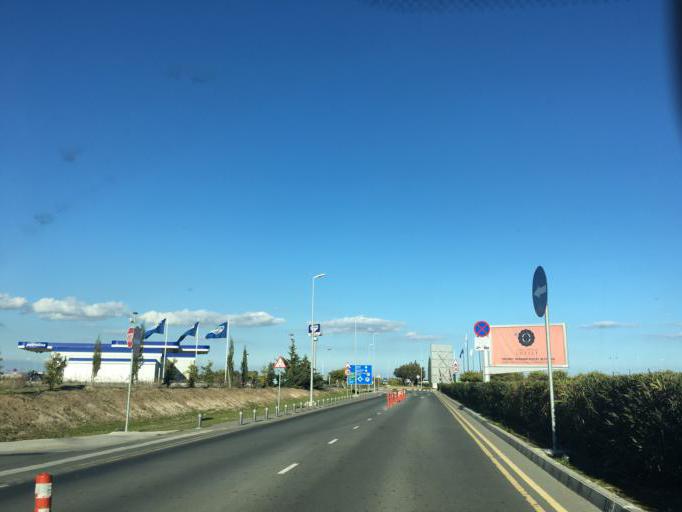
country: CY
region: Larnaka
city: Meneou
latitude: 34.8722
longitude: 33.6044
